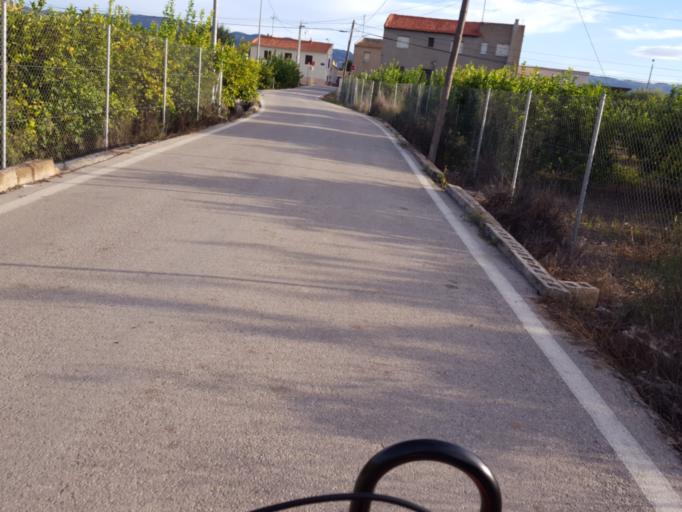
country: ES
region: Murcia
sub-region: Murcia
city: Murcia
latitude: 37.9903
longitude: -1.1686
